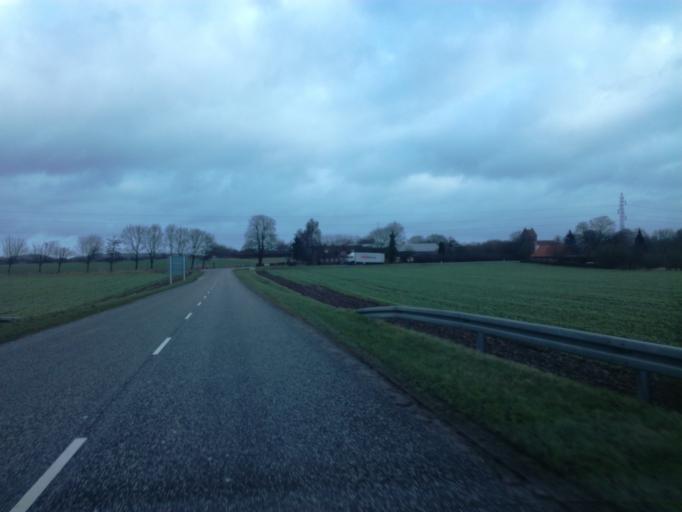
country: DK
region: South Denmark
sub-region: Vejle Kommune
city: Brejning
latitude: 55.6343
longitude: 9.6873
